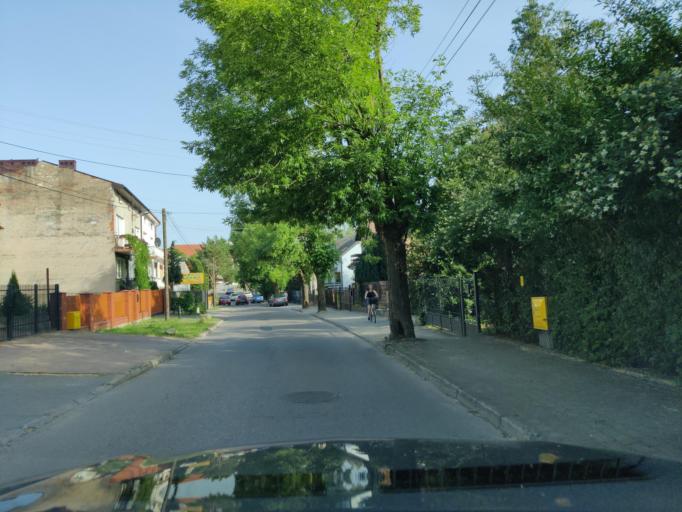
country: PL
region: Masovian Voivodeship
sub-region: Powiat wyszkowski
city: Wyszkow
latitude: 52.5959
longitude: 21.4590
